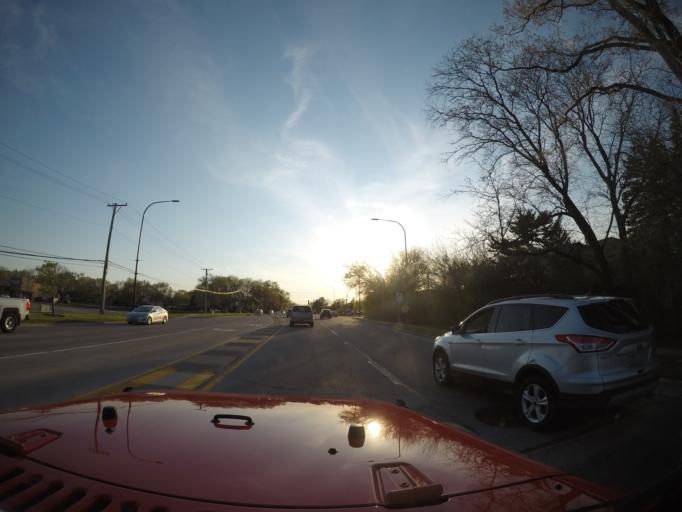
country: US
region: Illinois
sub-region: Cook County
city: Prospect Heights
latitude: 42.0881
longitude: -87.9351
